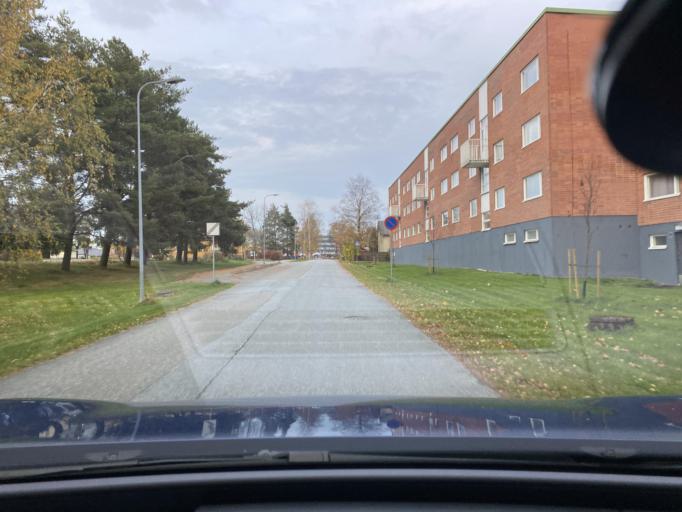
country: FI
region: Satakunta
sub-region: Pori
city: Huittinen
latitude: 61.1784
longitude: 22.6929
